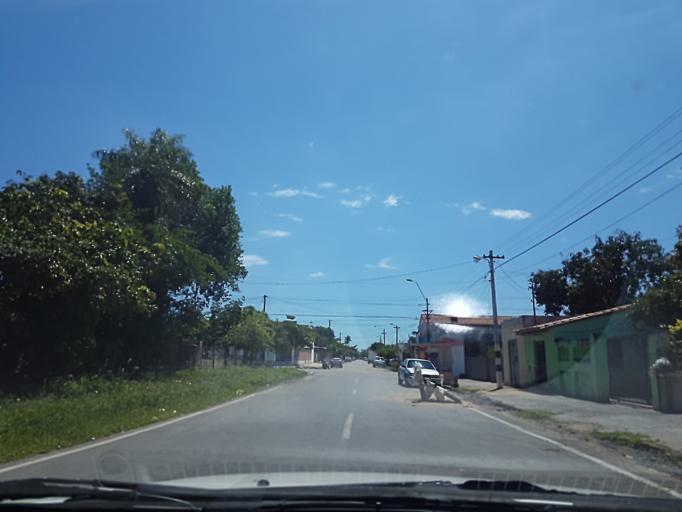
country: PY
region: Central
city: Colonia Mariano Roque Alonso
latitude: -25.2105
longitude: -57.5331
